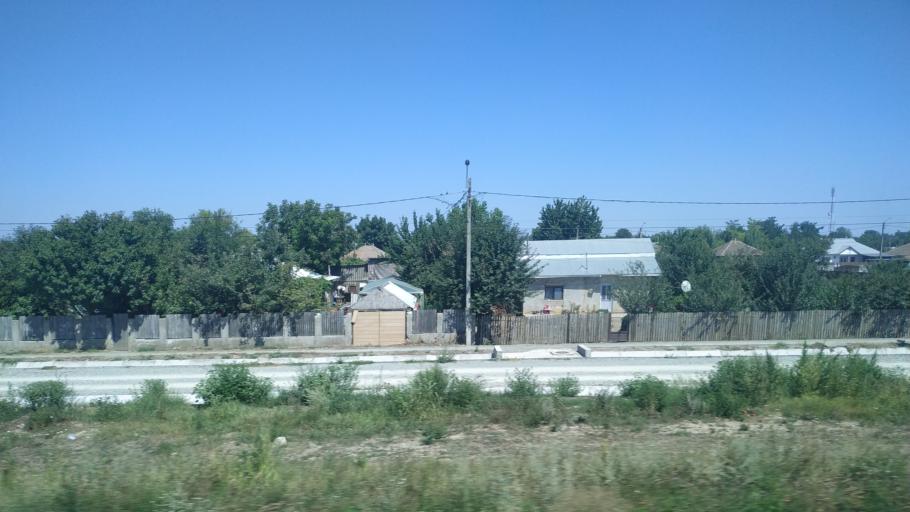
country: RO
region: Calarasi
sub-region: Comuna Perisoru
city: Perisoru
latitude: 44.4216
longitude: 27.6327
